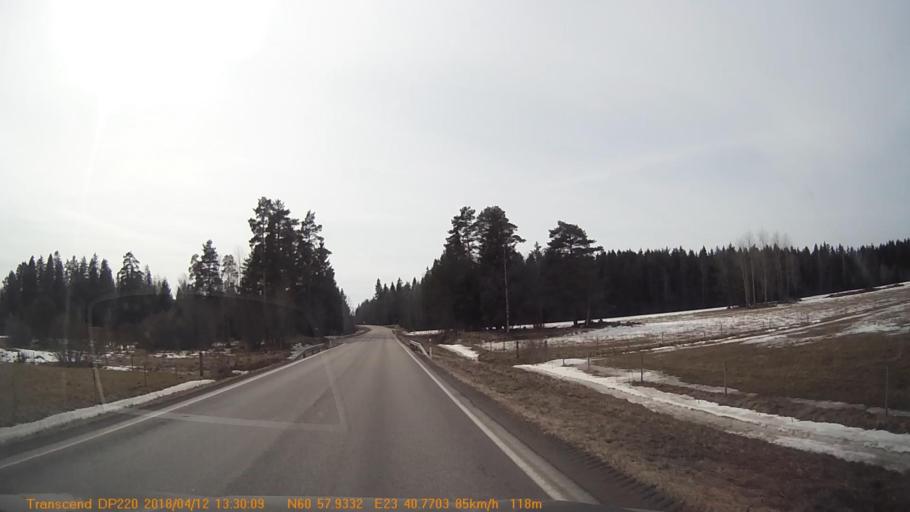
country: FI
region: Haeme
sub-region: Forssa
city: Forssa
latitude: 60.9655
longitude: 23.6796
